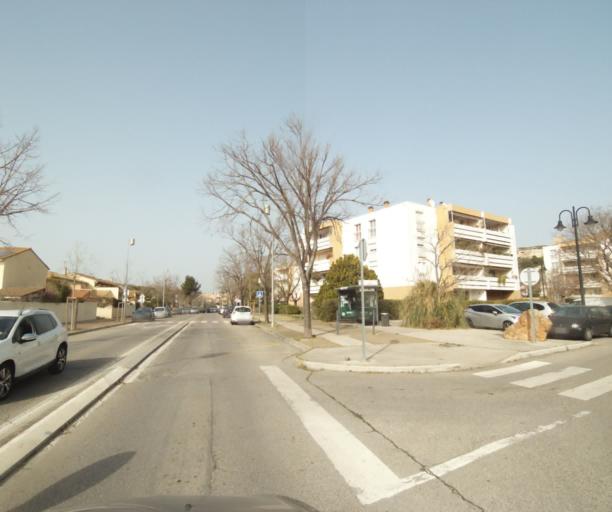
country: FR
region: Provence-Alpes-Cote d'Azur
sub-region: Departement des Bouches-du-Rhone
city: Vitrolles
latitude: 43.4598
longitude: 5.2424
